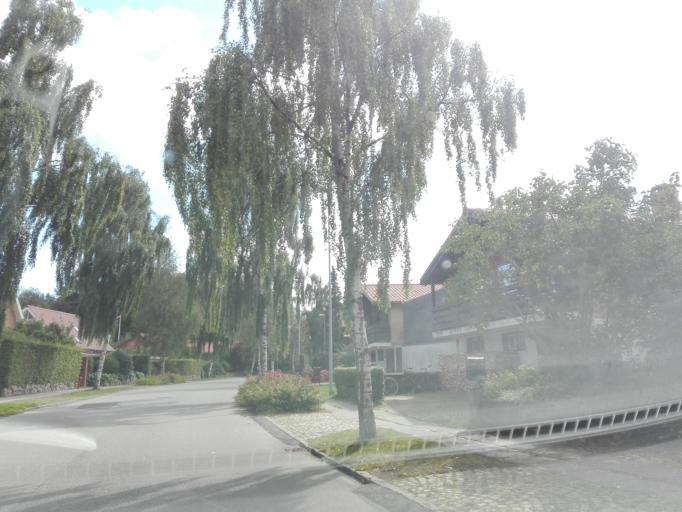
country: DK
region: Central Jutland
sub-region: Arhus Kommune
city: Arhus
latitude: 56.1178
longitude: 10.1872
